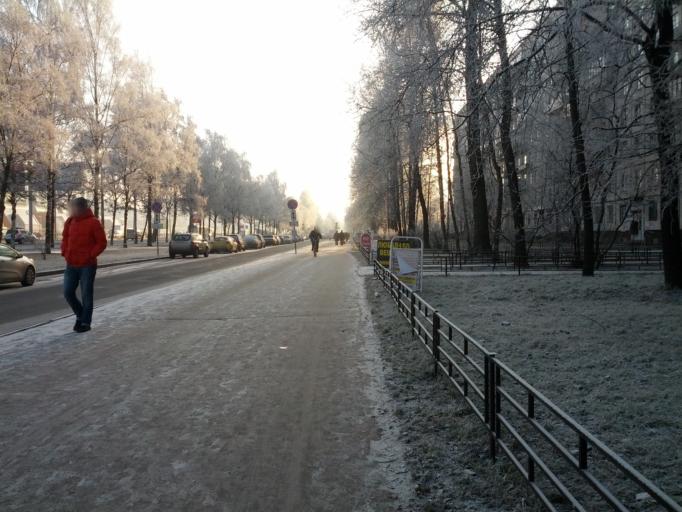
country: RU
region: Leningrad
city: Rybatskoye
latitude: 59.9039
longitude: 30.4844
